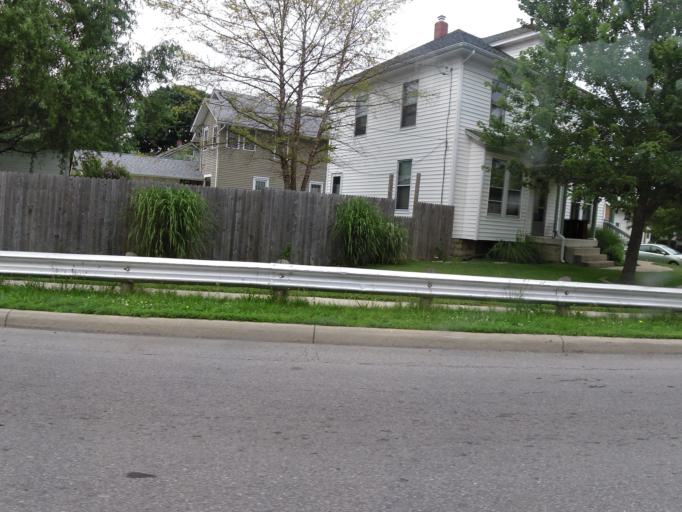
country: US
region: Ohio
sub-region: Clinton County
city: Wilmington
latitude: 39.4539
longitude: -83.8285
